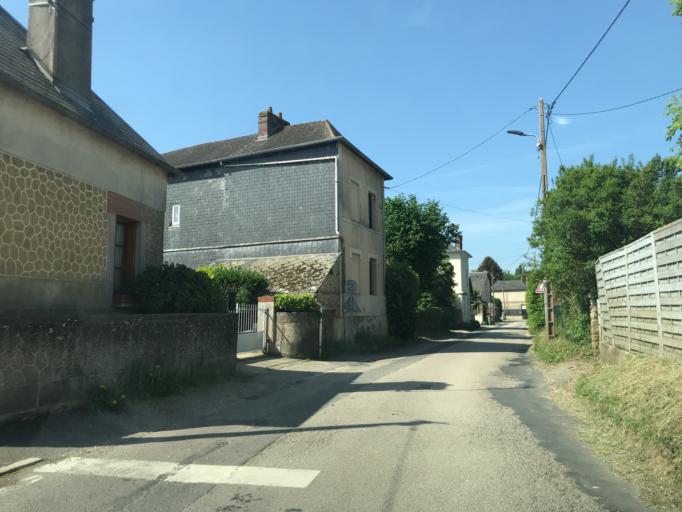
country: FR
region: Haute-Normandie
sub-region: Departement de la Seine-Maritime
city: Les Authieux-sur-le-Port-Saint-Ouen
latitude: 49.3549
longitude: 1.1512
